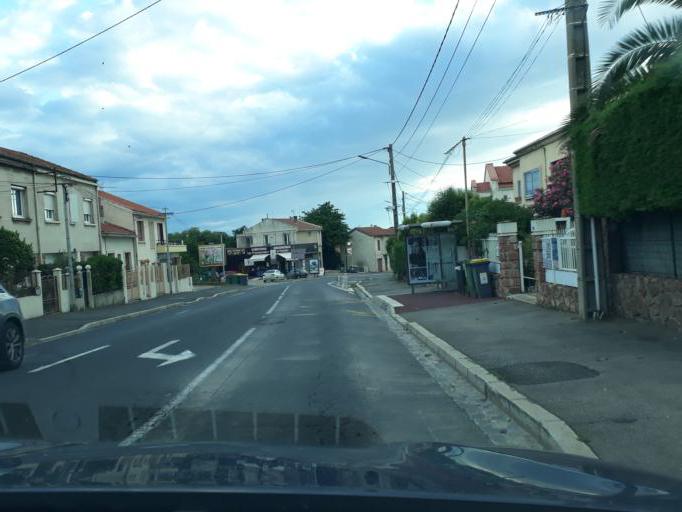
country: FR
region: Languedoc-Roussillon
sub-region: Departement de l'Herault
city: Beziers
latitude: 43.3349
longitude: 3.2349
